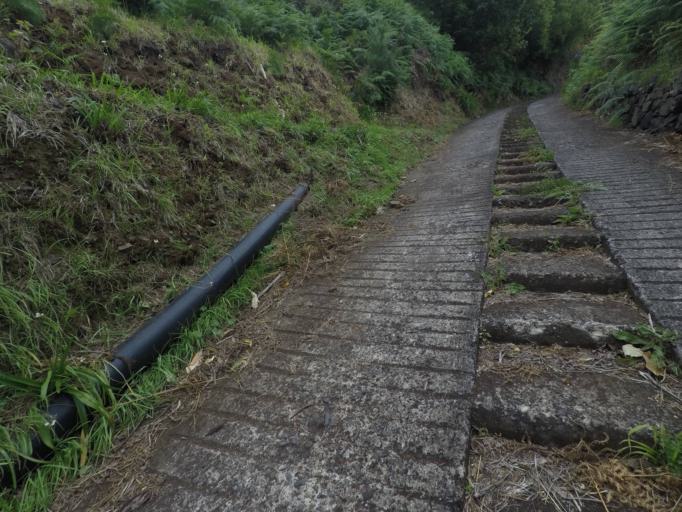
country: PT
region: Madeira
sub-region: Santana
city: Santana
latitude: 32.7879
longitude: -16.8588
